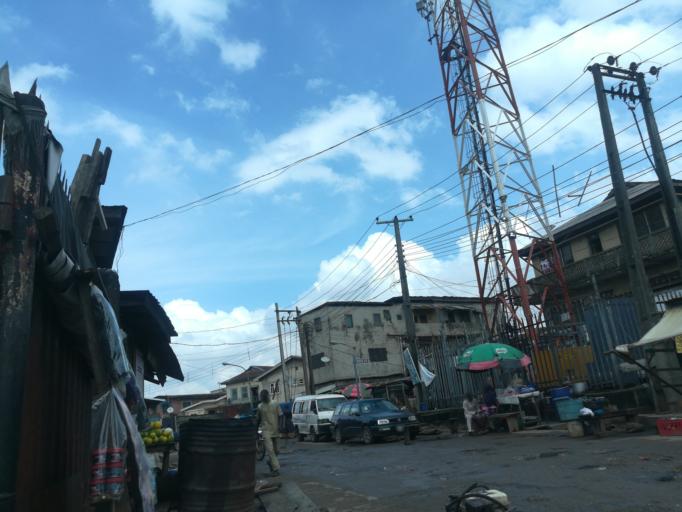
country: NG
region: Lagos
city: Somolu
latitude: 6.5360
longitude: 3.3639
